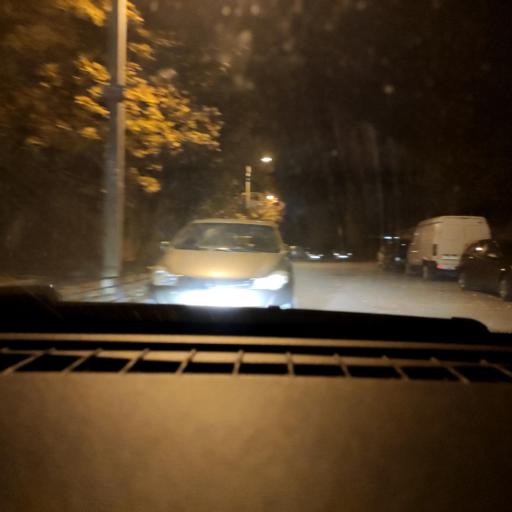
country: RU
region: Voronezj
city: Voronezh
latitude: 51.6352
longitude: 39.2444
